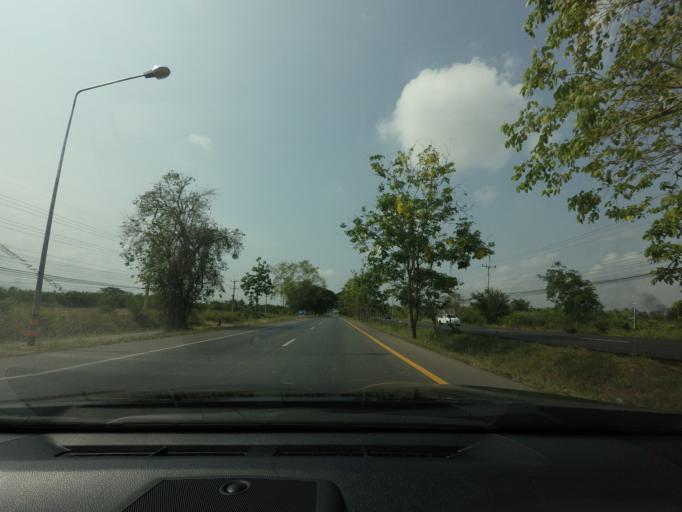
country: TH
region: Prachuap Khiri Khan
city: Sam Roi Yot
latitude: 12.2779
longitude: 99.8718
